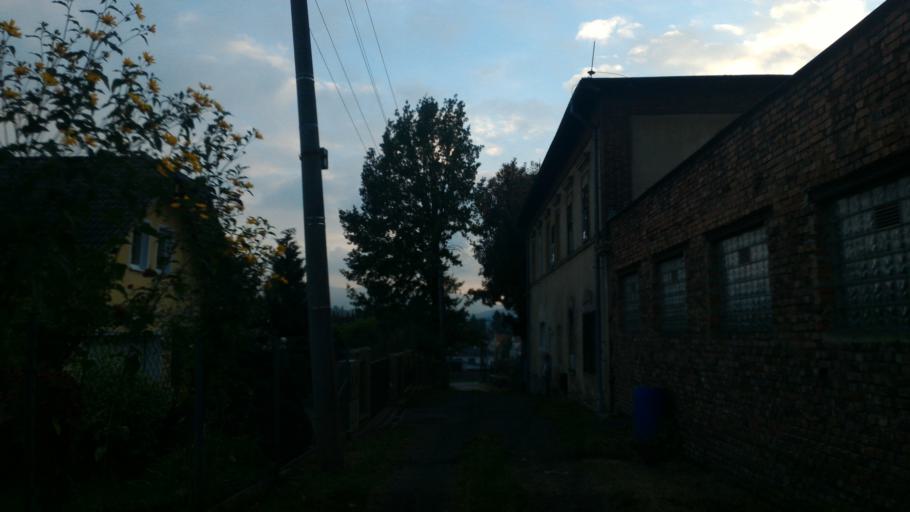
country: CZ
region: Ustecky
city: Varnsdorf
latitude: 50.9113
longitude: 14.6371
